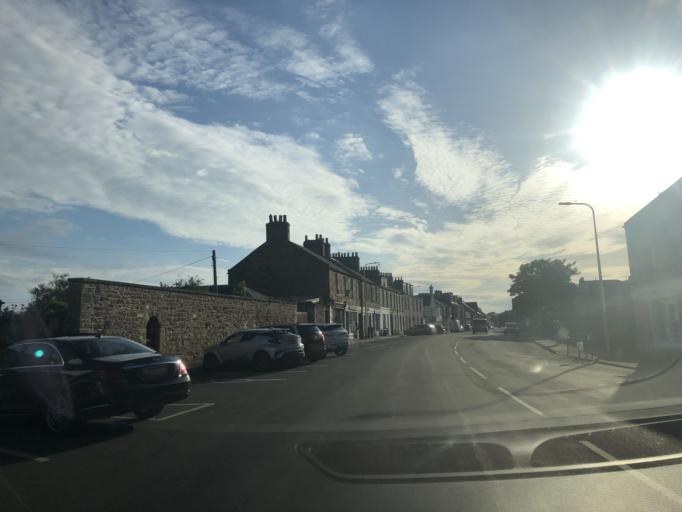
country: GB
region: Scotland
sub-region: Fife
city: Saint Monance
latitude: 56.1905
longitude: -2.8195
